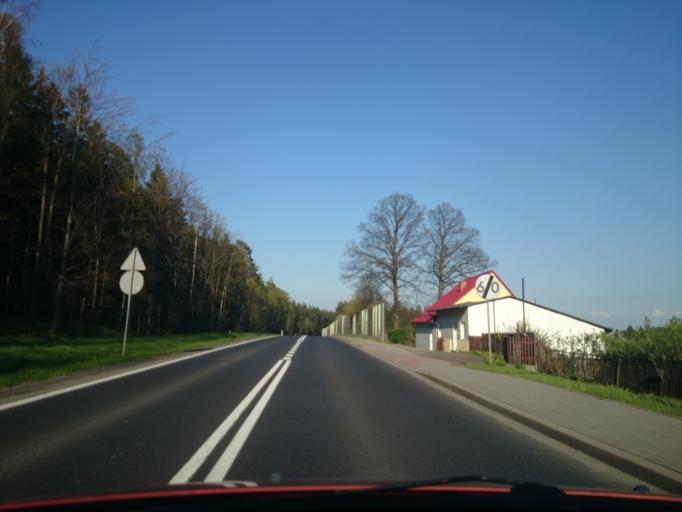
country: PL
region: Lower Silesian Voivodeship
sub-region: Powiat klodzki
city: Szczytna
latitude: 50.4252
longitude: 16.4704
